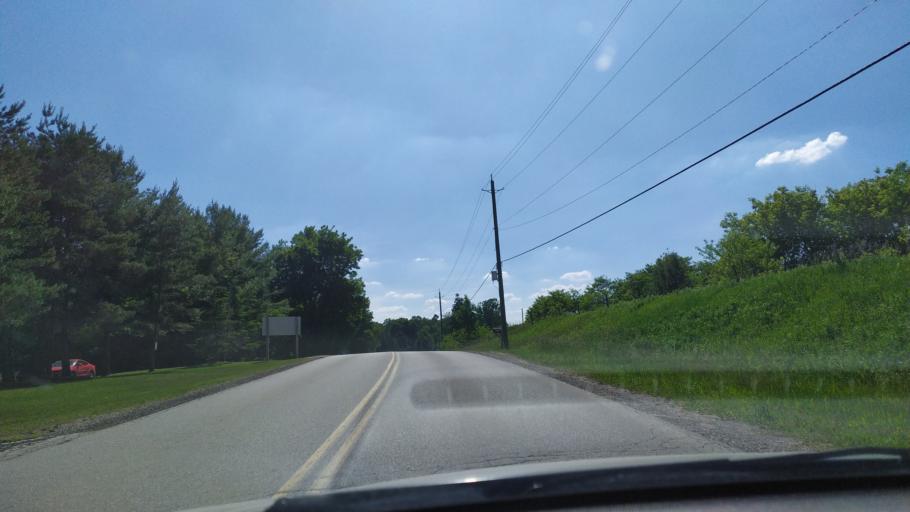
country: CA
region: Ontario
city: Kitchener
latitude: 43.3704
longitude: -80.5653
